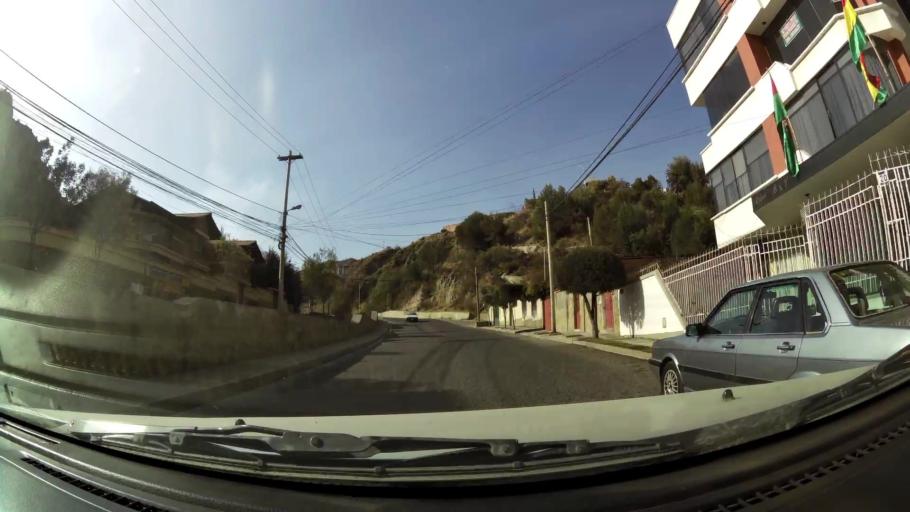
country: BO
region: La Paz
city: La Paz
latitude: -16.5294
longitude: -68.0784
